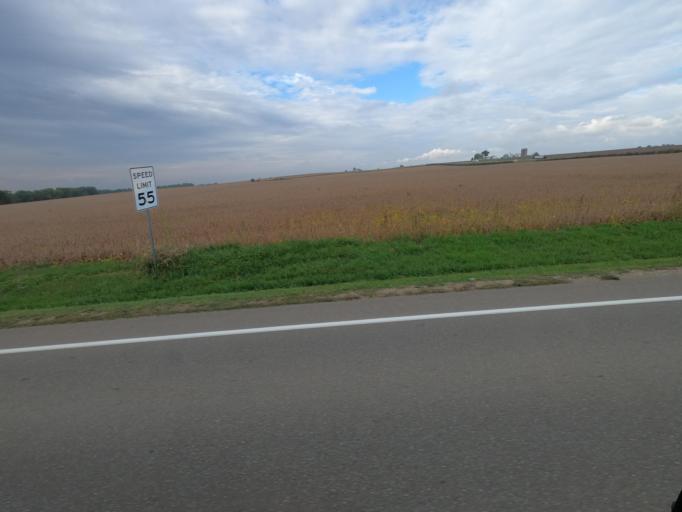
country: US
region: Iowa
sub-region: Henry County
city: Mount Pleasant
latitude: 40.7845
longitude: -91.5675
